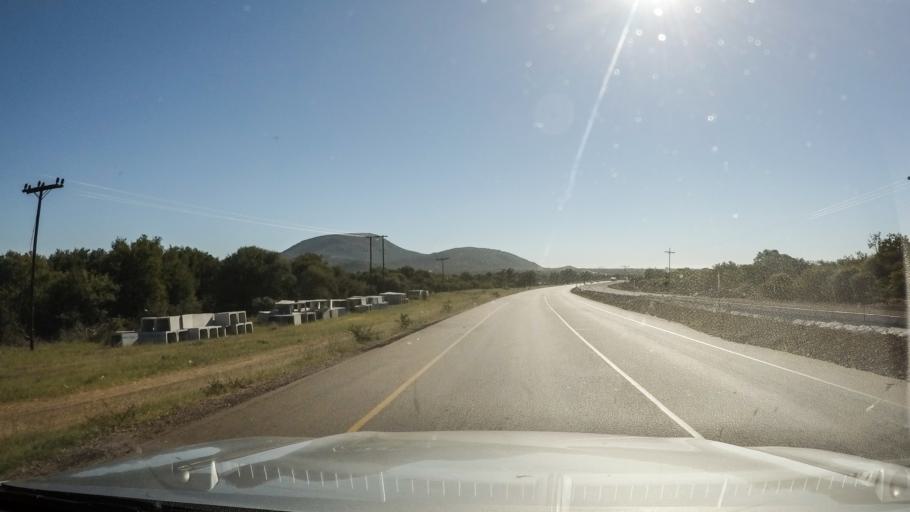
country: BW
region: Kweneng
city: Gabane
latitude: -24.7436
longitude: 25.8319
